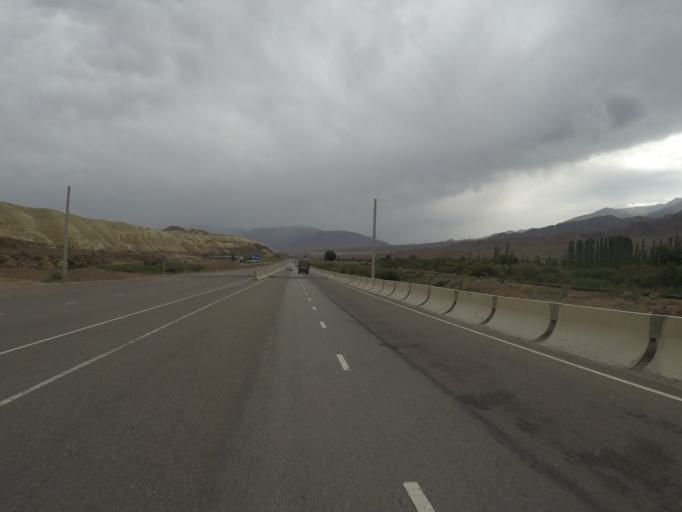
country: KG
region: Chuy
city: Bystrovka
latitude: 42.5289
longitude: 75.8212
